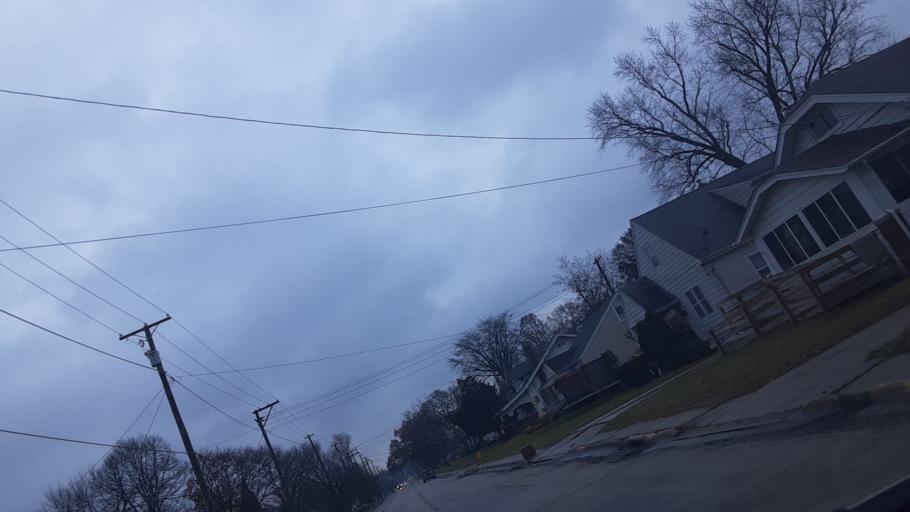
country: US
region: Illinois
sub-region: Winnebago County
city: Loves Park
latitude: 42.3106
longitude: -89.0539
